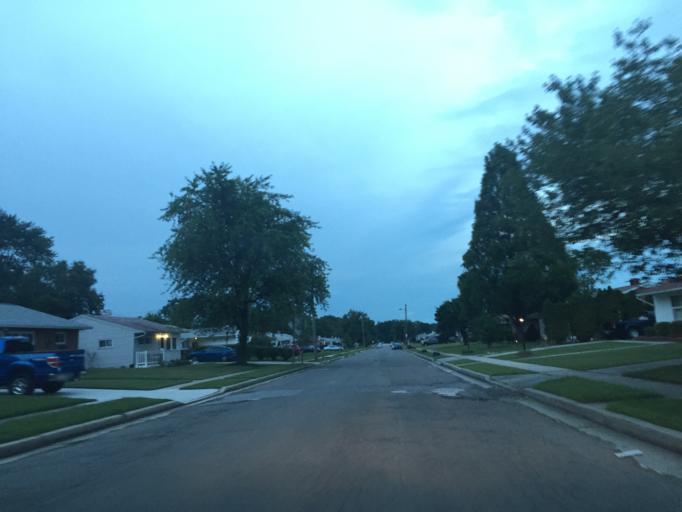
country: US
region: Maryland
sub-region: Baltimore County
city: Carney
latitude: 39.3940
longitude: -76.5399
